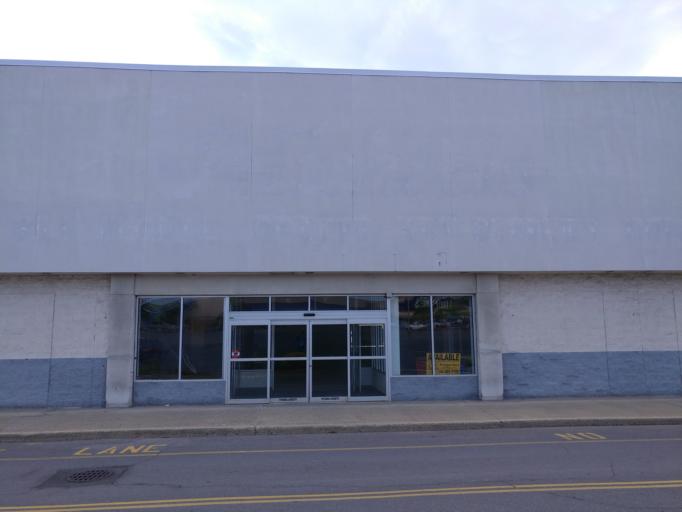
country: US
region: New York
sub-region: Ulster County
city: Lake Katrine
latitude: 41.9723
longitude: -73.9847
